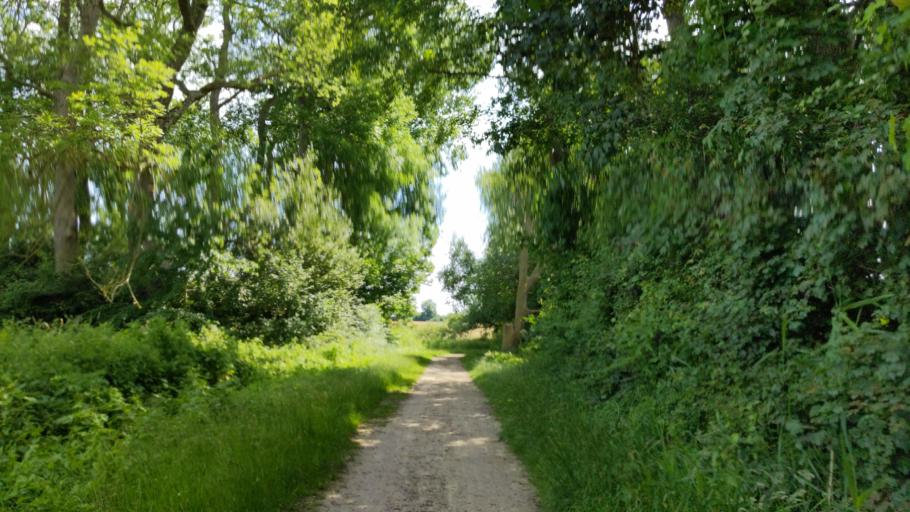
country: DE
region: Schleswig-Holstein
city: Eutin
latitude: 54.1379
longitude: 10.6350
